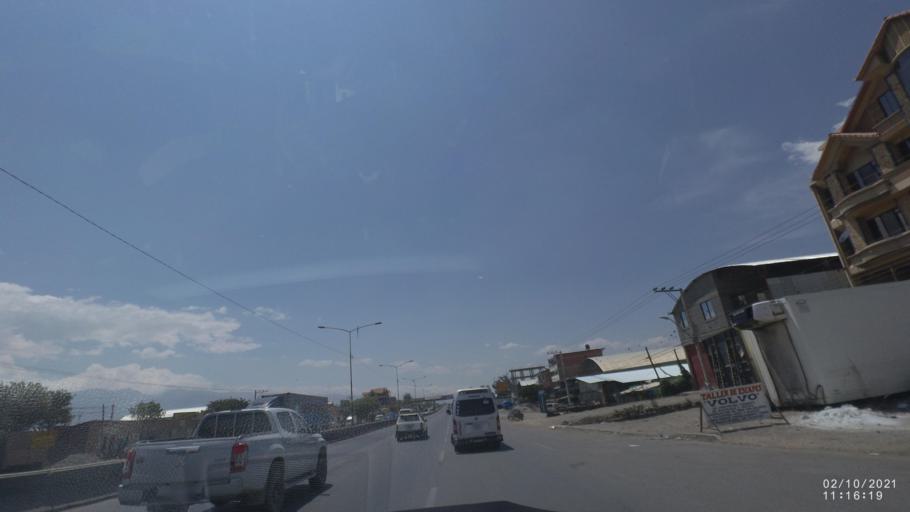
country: BO
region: Cochabamba
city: Sipe Sipe
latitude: -17.3953
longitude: -66.3008
